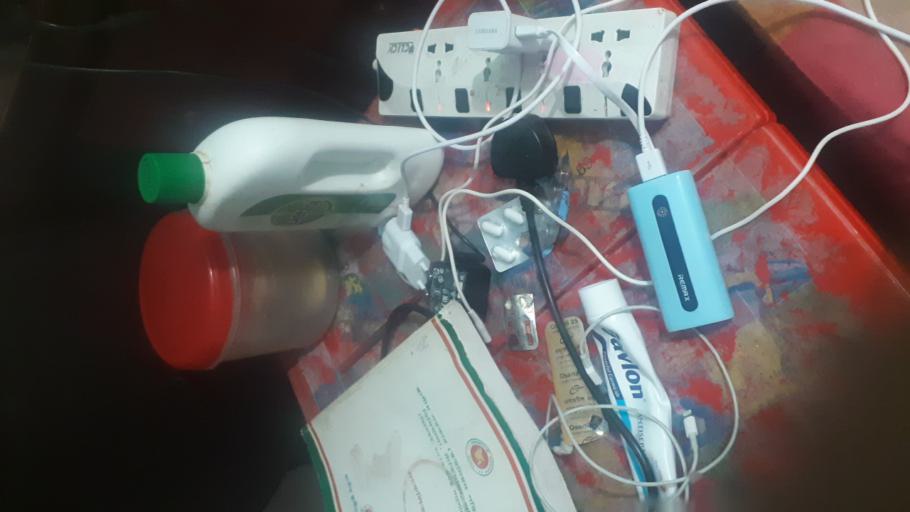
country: BD
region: Chittagong
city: Lakshmipur
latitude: 22.8750
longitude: 91.0995
